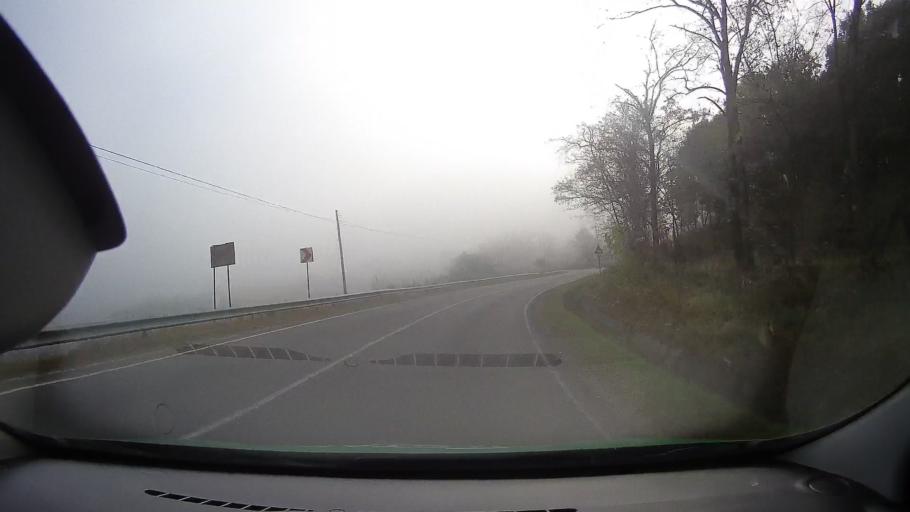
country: RO
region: Tulcea
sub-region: Municipiul Tulcea
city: Tulcea
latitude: 45.1665
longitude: 28.8400
